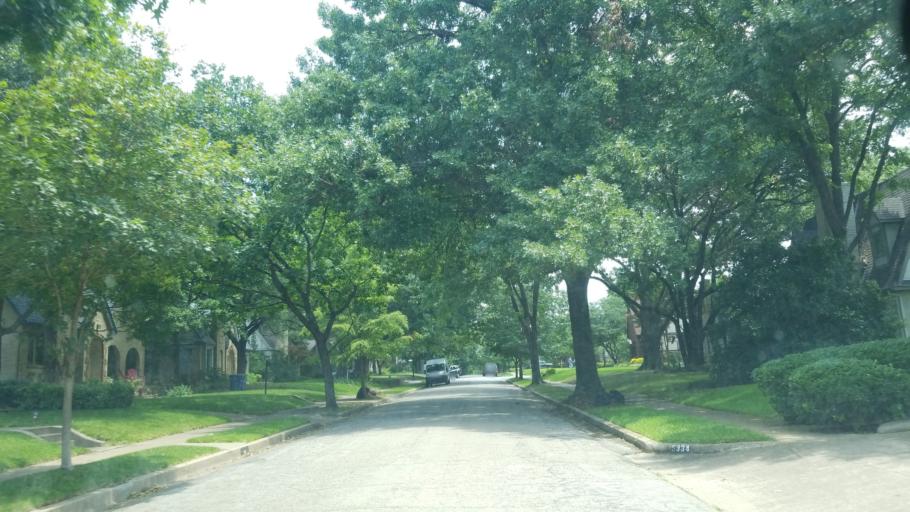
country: US
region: Texas
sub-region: Dallas County
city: Highland Park
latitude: 32.8282
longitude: -96.7784
